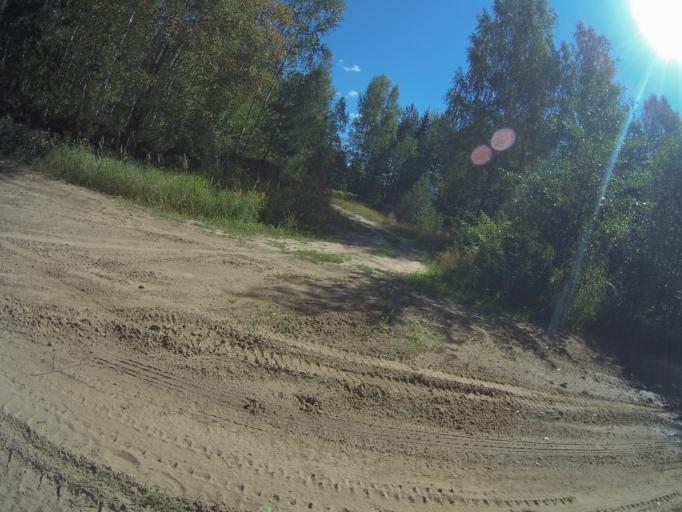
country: RU
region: Vladimir
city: Raduzhnyy
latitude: 55.9310
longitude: 40.2448
